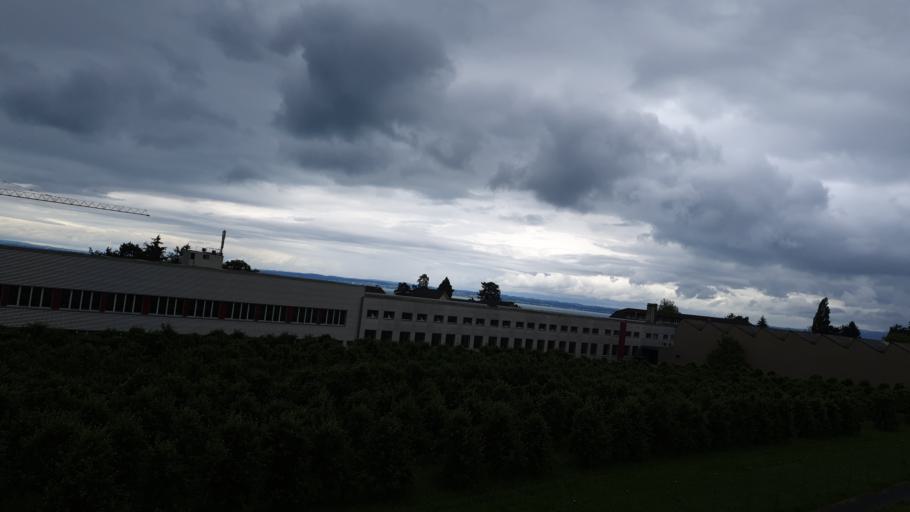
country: CH
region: Saint Gallen
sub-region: Wahlkreis Rorschach
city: Rorschach
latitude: 47.4768
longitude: 9.5181
